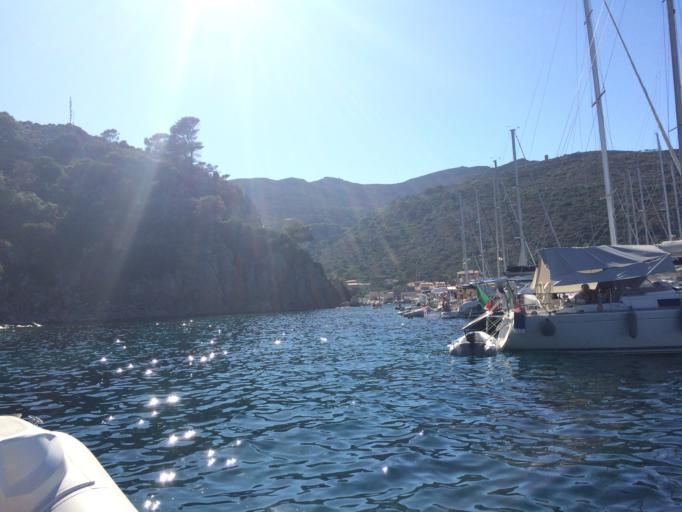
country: IT
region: Tuscany
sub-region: Provincia di Livorno
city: Capraia Isola
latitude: 43.0496
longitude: 9.8398
